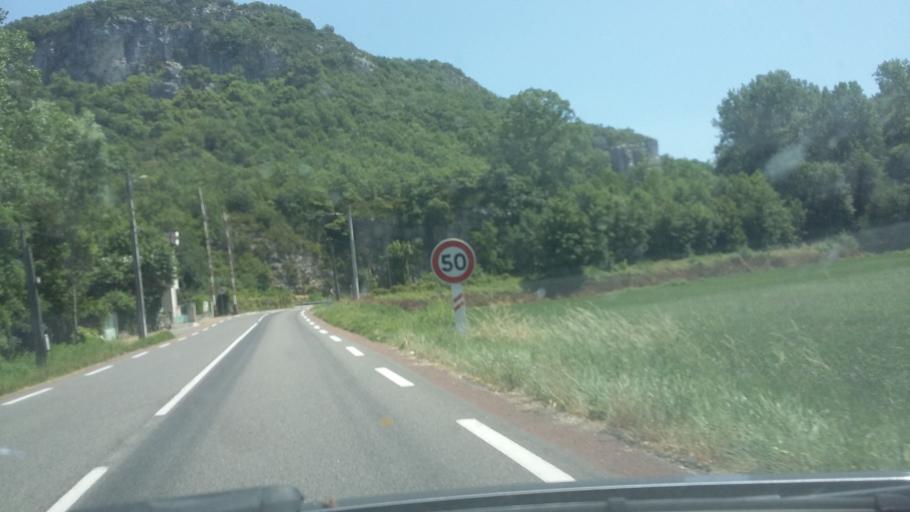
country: FR
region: Rhone-Alpes
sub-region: Departement de l'Ain
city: Virieu-le-Grand
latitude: 45.8204
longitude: 5.6532
